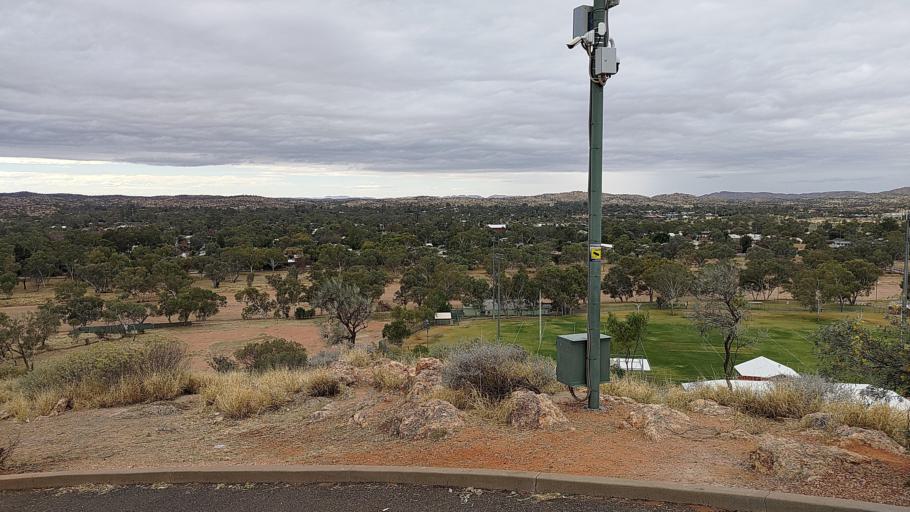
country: AU
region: Northern Territory
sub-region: Alice Springs
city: Alice Springs
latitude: -23.6947
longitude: 133.8823
